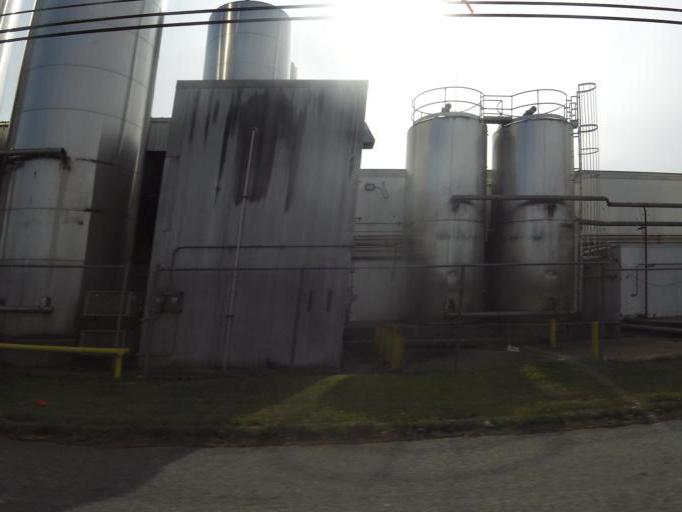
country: US
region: Alabama
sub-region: Houston County
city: Cowarts
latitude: 31.1940
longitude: -85.3212
